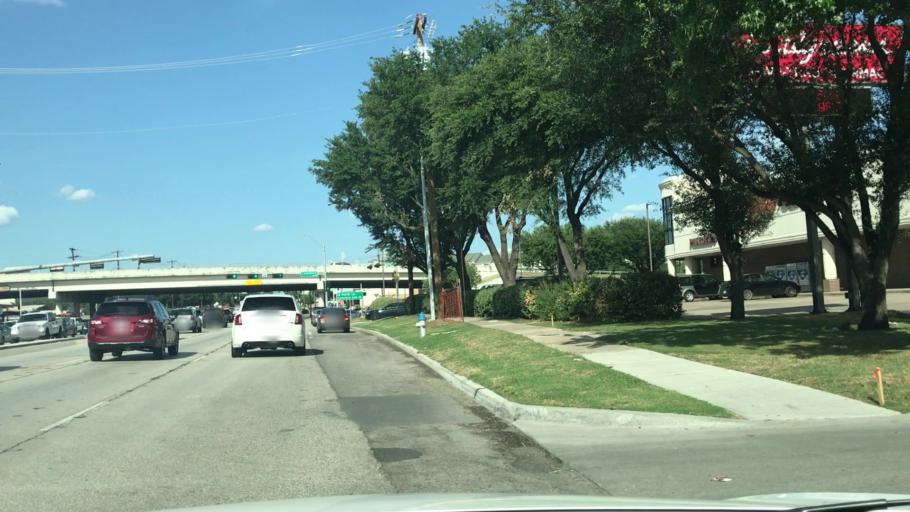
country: US
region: Texas
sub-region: Dallas County
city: University Park
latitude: 32.8606
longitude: -96.8565
